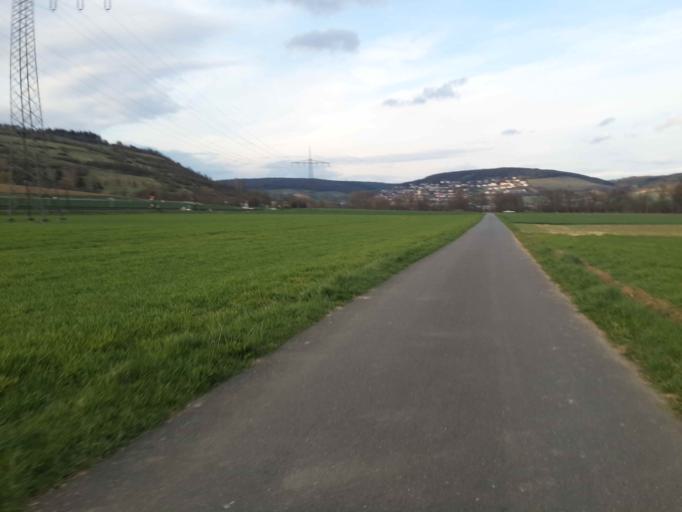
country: DE
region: Baden-Wuerttemberg
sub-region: Regierungsbezirk Stuttgart
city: Lauda-Konigshofen
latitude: 49.5323
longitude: 9.7145
